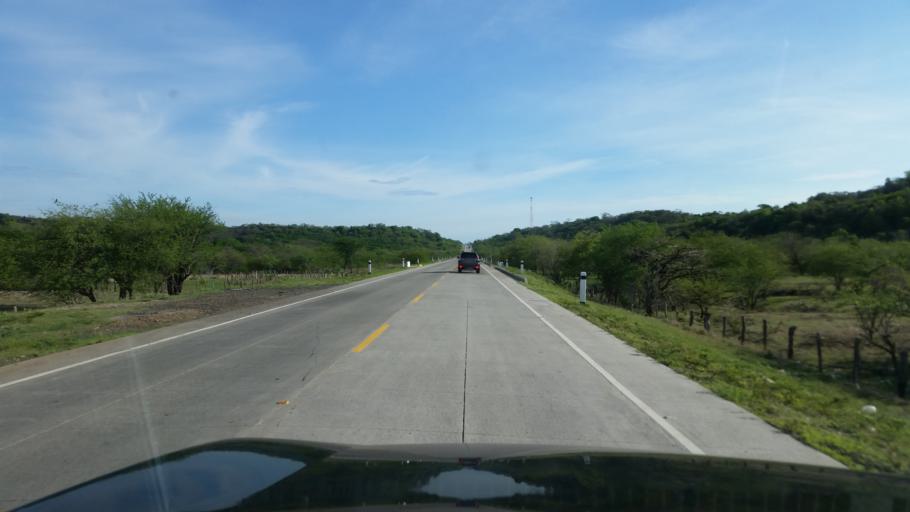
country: NI
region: Leon
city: Nagarote
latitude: 12.1943
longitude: -86.6778
